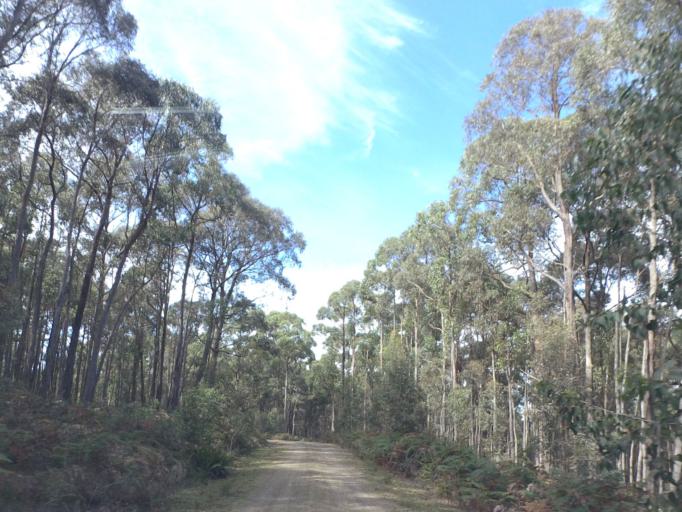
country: AU
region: Victoria
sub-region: Moorabool
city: Bacchus Marsh
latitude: -37.4379
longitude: 144.2661
